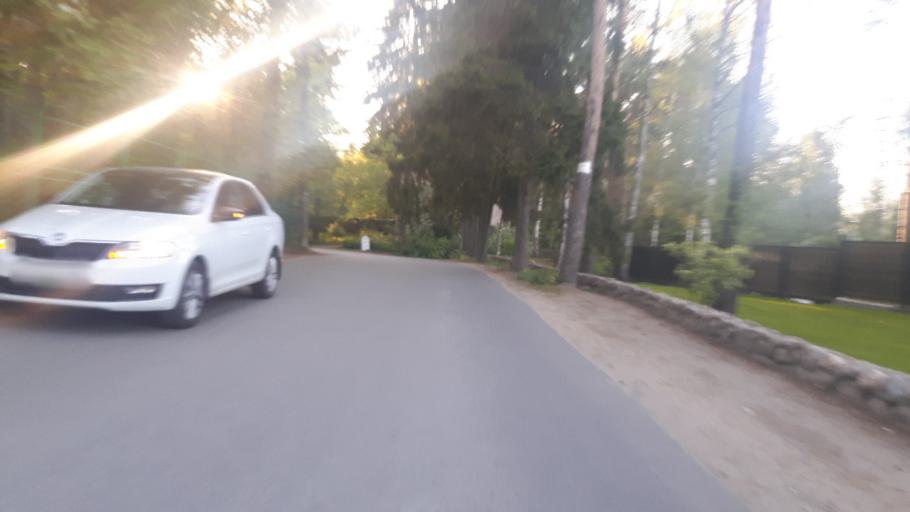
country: RU
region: St.-Petersburg
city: Zelenogorsk
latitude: 60.1956
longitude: 29.6647
